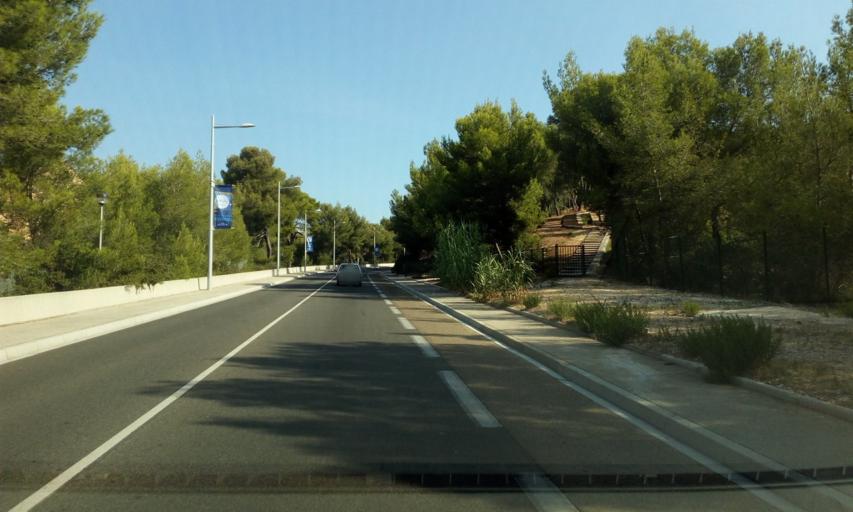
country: FR
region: Provence-Alpes-Cote d'Azur
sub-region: Departement du Var
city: Bandol
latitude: 43.1444
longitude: 5.7477
